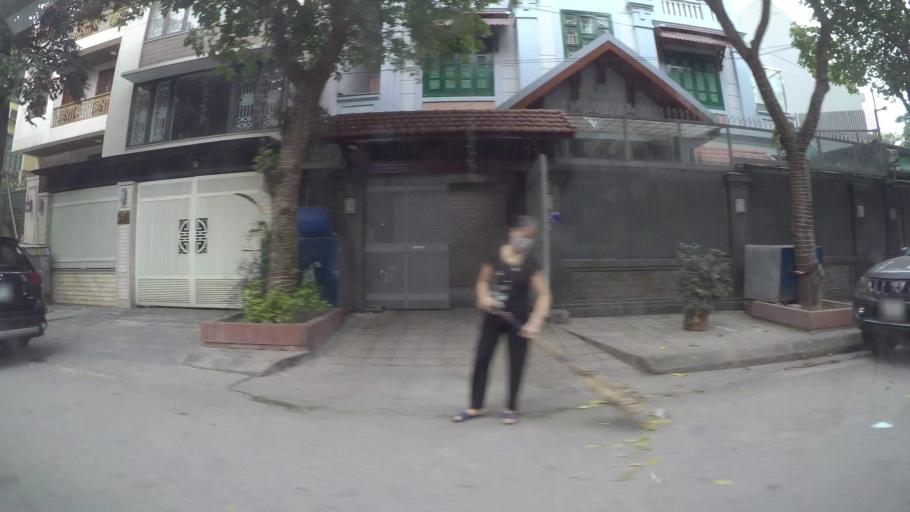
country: VN
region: Ha Noi
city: Cau Dien
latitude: 21.0303
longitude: 105.7655
